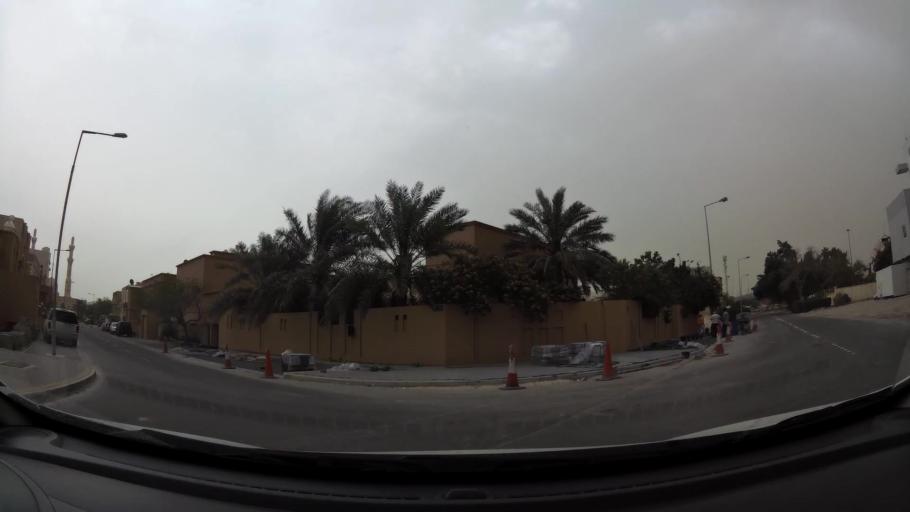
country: BH
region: Northern
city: Madinat `Isa
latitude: 26.1709
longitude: 50.5437
